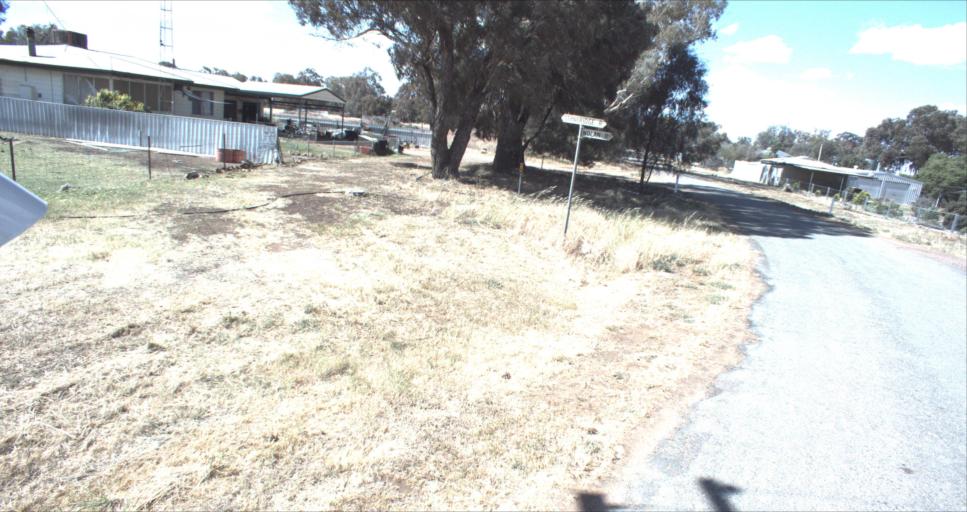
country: AU
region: New South Wales
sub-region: Leeton
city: Leeton
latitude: -34.5170
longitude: 146.2325
